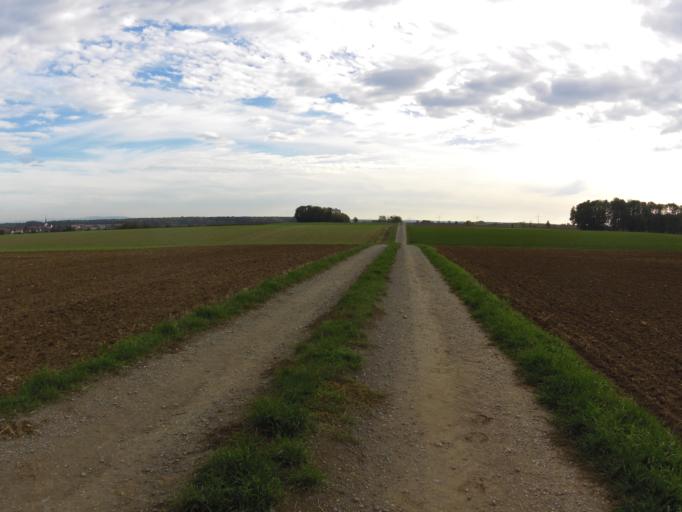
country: DE
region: Bavaria
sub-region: Regierungsbezirk Unterfranken
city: Biebelried
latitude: 49.7357
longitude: 10.0720
